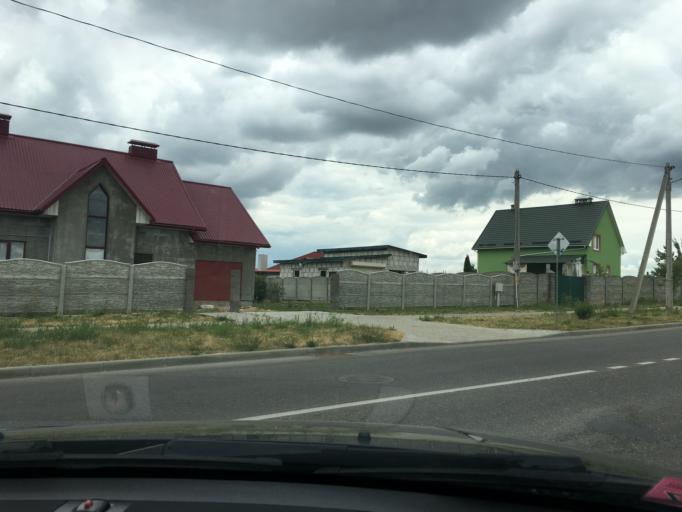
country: BY
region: Grodnenskaya
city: Hrodna
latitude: 53.6197
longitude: 23.8303
